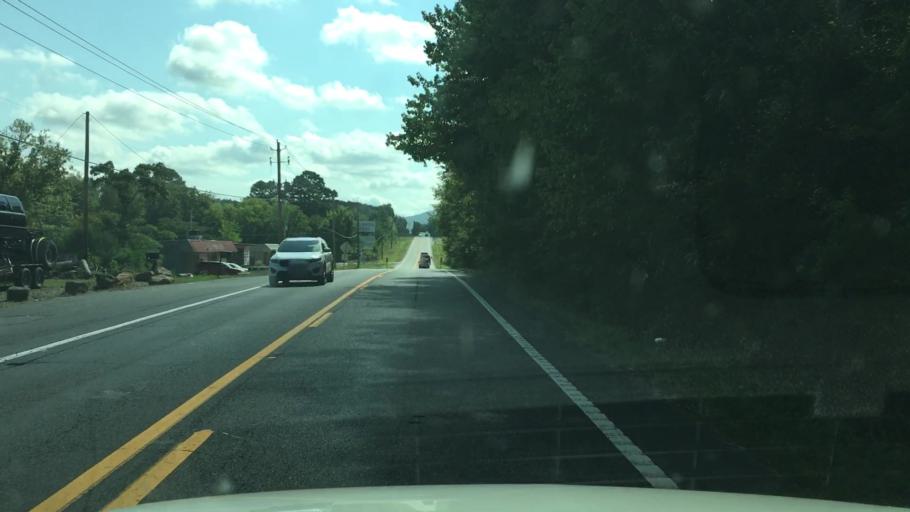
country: US
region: Arkansas
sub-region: Garland County
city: Piney
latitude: 34.5094
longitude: -93.1649
